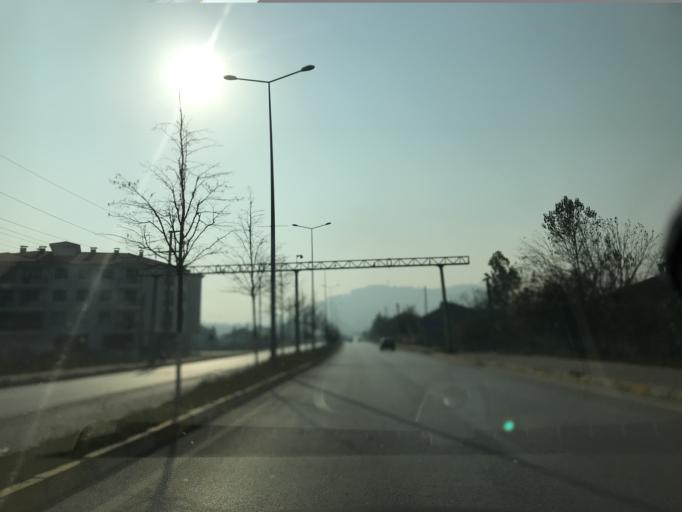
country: TR
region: Duzce
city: Cumayeri
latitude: 40.8616
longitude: 30.9535
